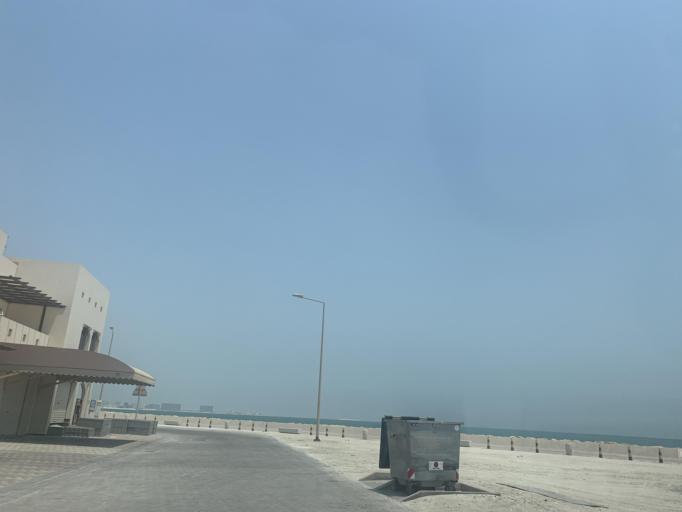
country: BH
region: Muharraq
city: Al Hadd
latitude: 26.2359
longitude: 50.6784
